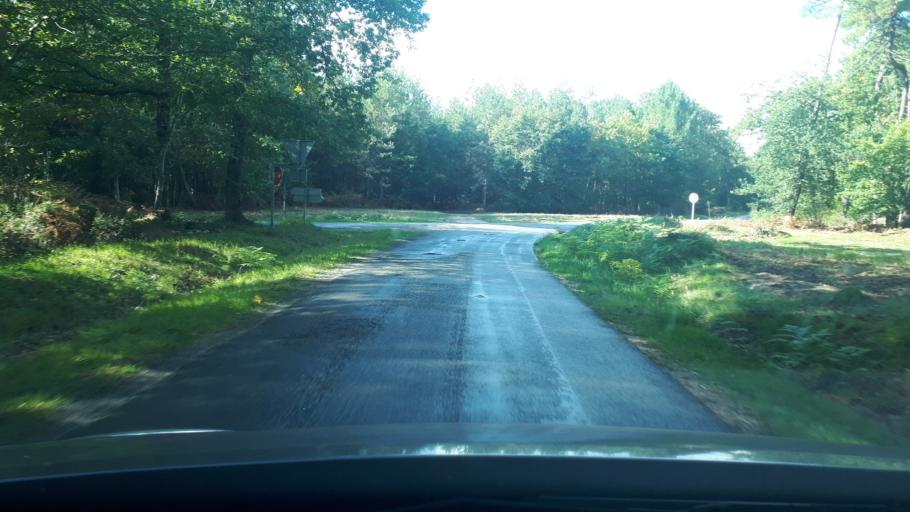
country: FR
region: Centre
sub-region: Departement du Loir-et-Cher
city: Saint-Romain-sur-Cher
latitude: 47.3474
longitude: 1.3647
